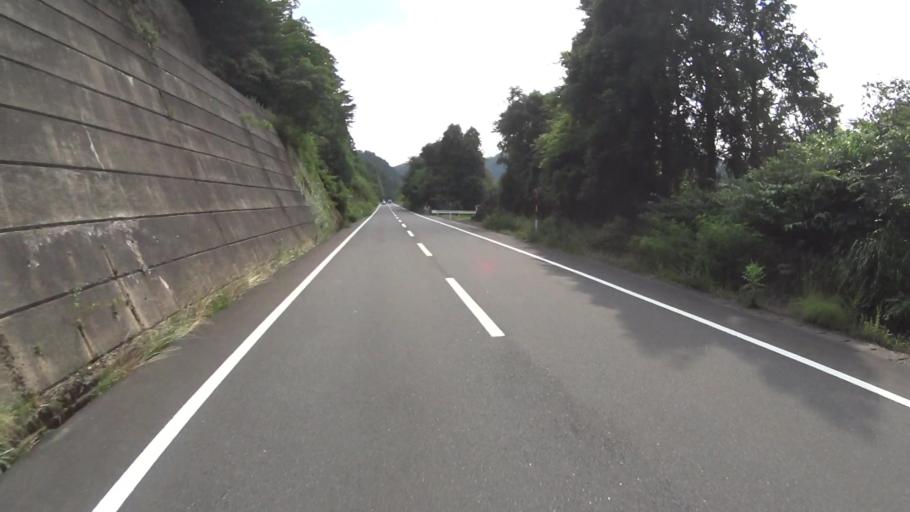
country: JP
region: Kyoto
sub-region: Kyoto-shi
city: Kamigyo-ku
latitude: 35.2188
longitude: 135.6490
